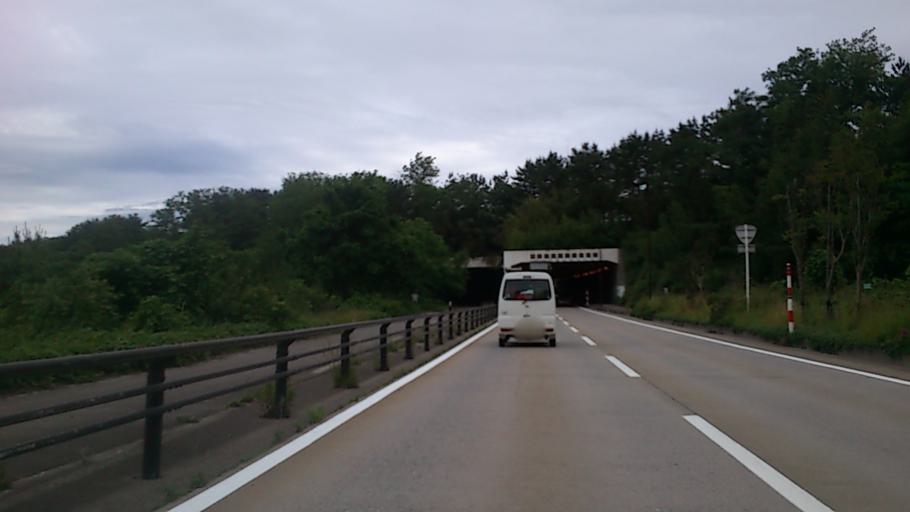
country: JP
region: Akita
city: Akita Shi
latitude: 39.7144
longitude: 140.0781
